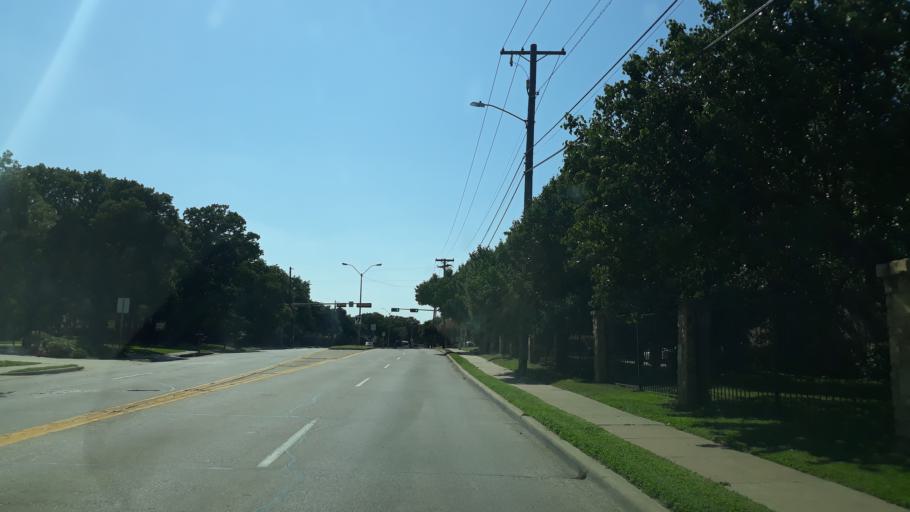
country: US
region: Texas
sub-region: Dallas County
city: Irving
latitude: 32.8293
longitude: -96.9997
